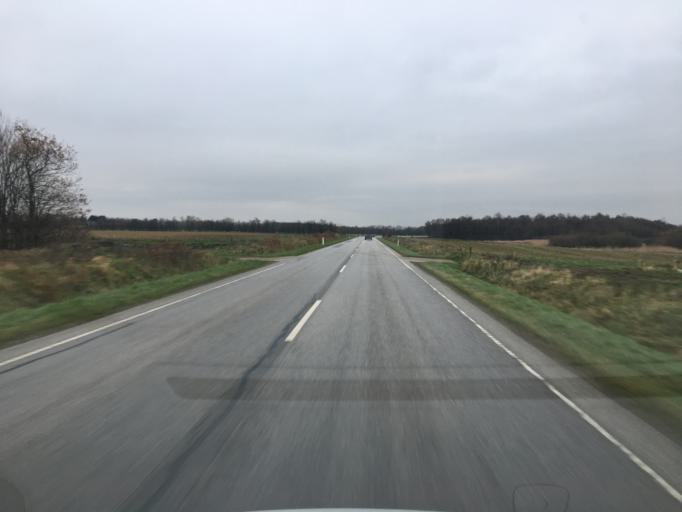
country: DK
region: South Denmark
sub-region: Aabenraa Kommune
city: Tinglev
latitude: 55.0002
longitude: 9.2398
